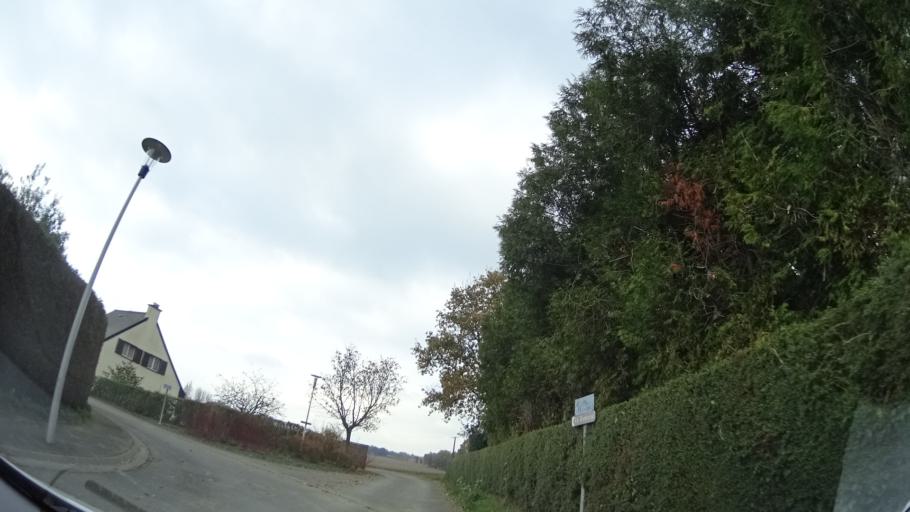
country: FR
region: Brittany
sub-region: Departement d'Ille-et-Vilaine
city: Montgermont
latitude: 48.1608
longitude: -1.7145
